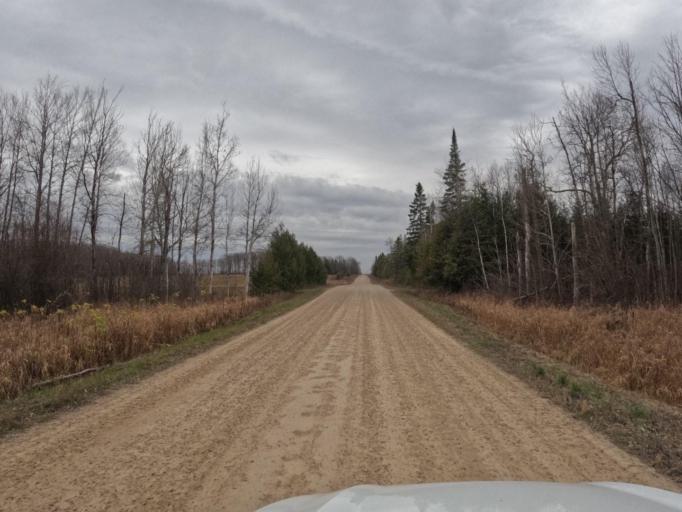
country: CA
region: Ontario
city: Shelburne
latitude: 44.0279
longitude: -80.3935
